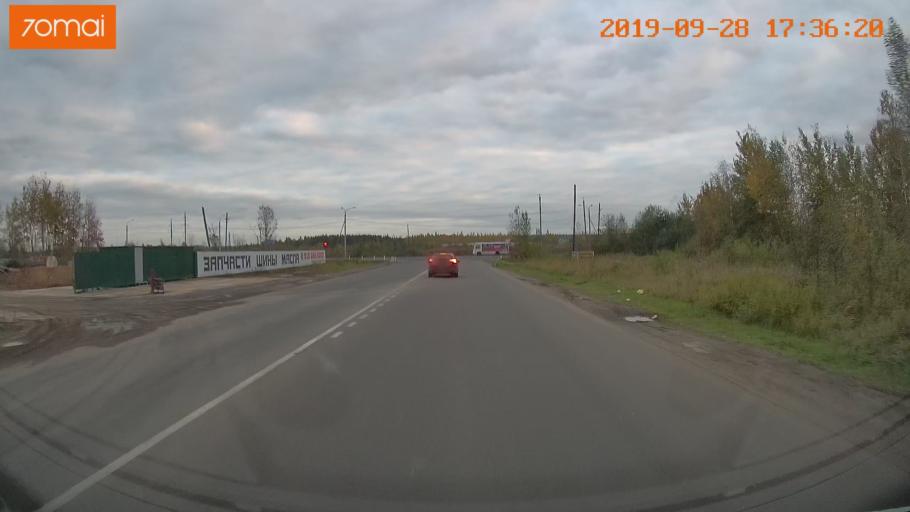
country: RU
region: Jaroslavl
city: Yaroslavl
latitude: 57.5432
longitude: 39.9668
